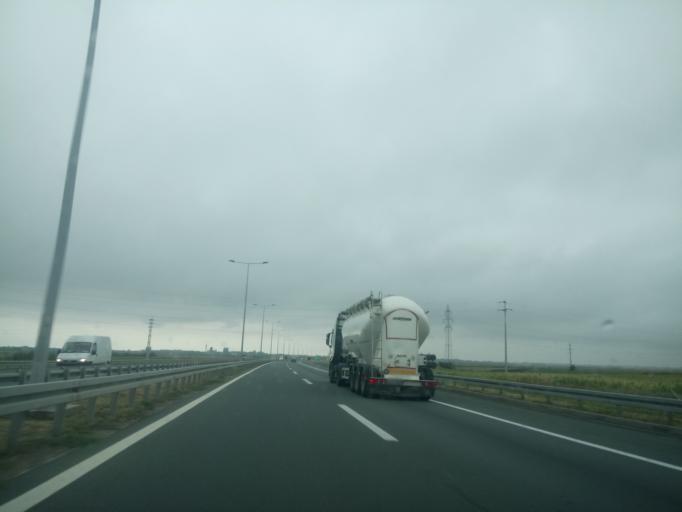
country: RS
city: Dobanovci
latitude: 44.8796
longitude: 20.2702
